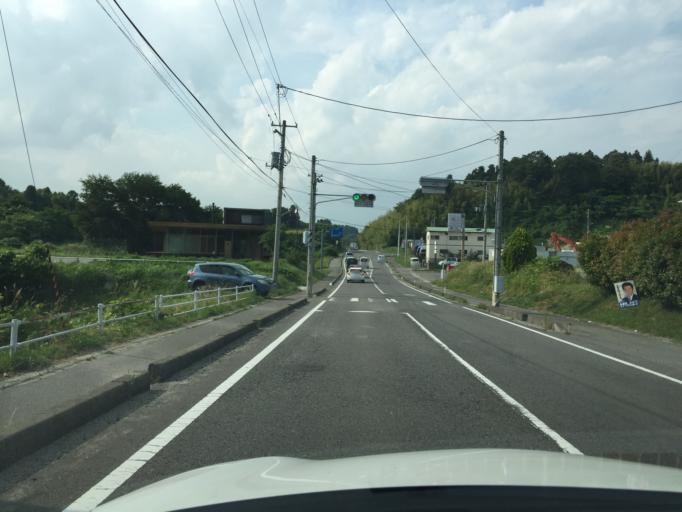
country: JP
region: Fukushima
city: Miharu
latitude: 37.4267
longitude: 140.4471
